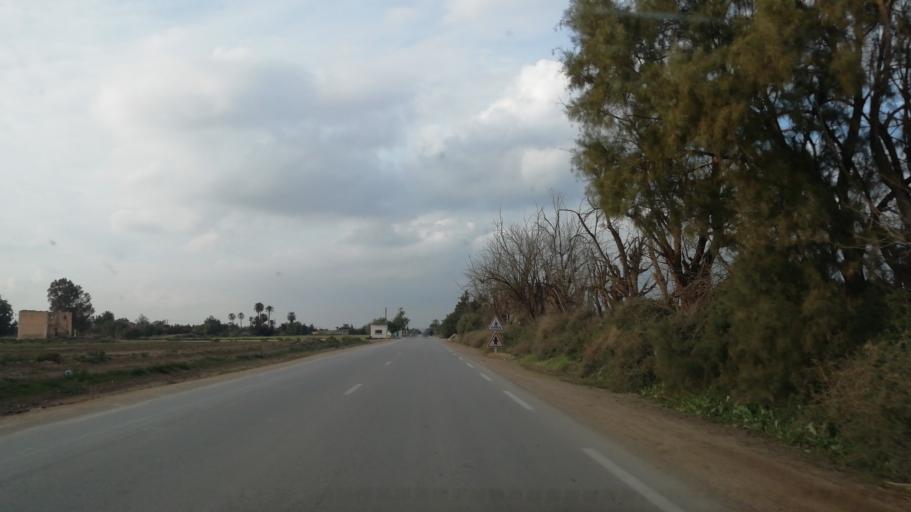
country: DZ
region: Mascara
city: Sig
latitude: 35.6835
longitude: -0.0125
